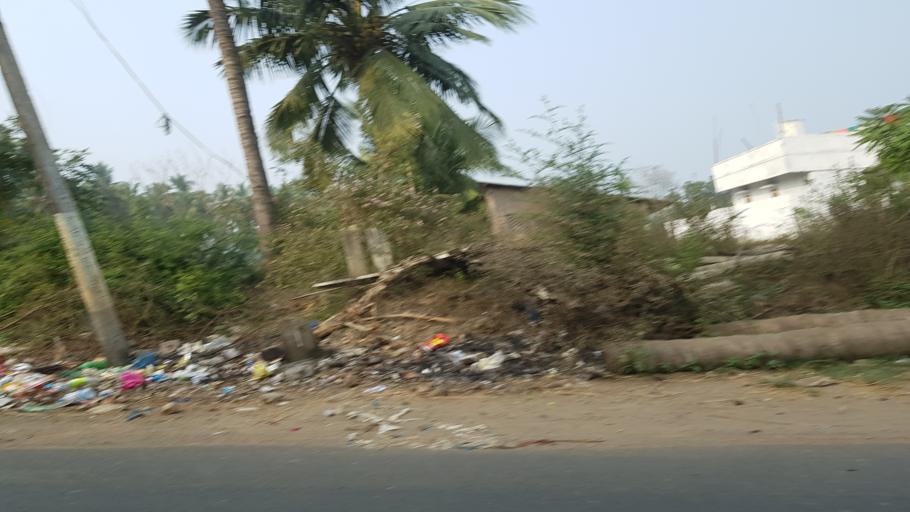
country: IN
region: Andhra Pradesh
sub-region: West Godavari
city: Akividu
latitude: 16.5377
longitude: 81.4175
